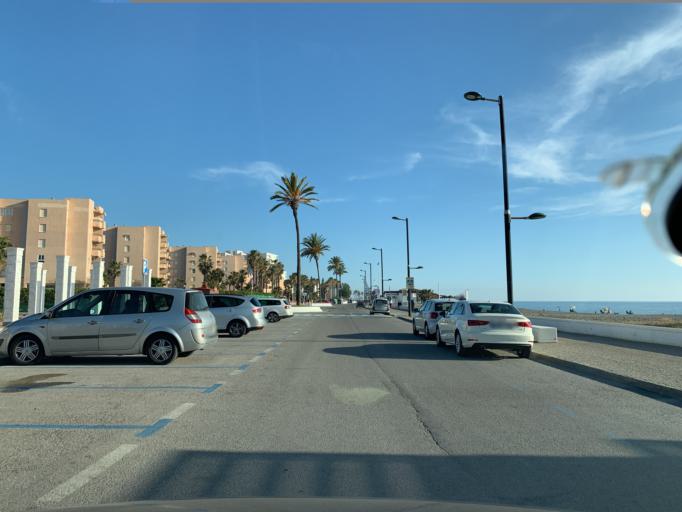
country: ES
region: Andalusia
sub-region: Provincia de Granada
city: Salobrena
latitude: 36.7313
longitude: -3.5867
